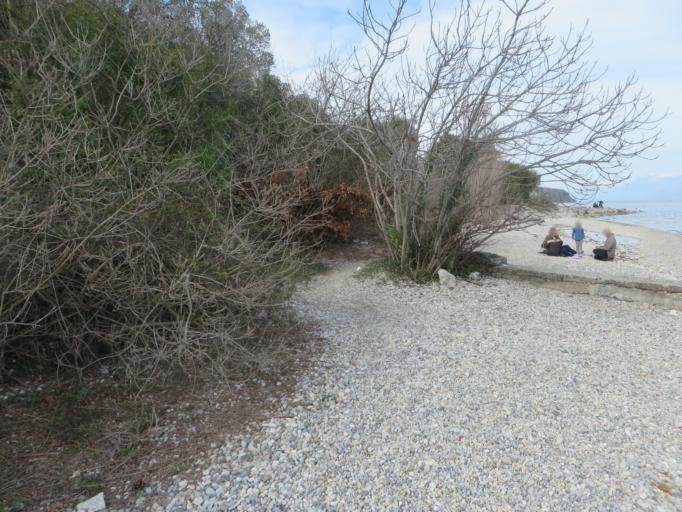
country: IT
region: Lombardy
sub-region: Provincia di Brescia
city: Solarolo
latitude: 45.5301
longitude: 10.5584
